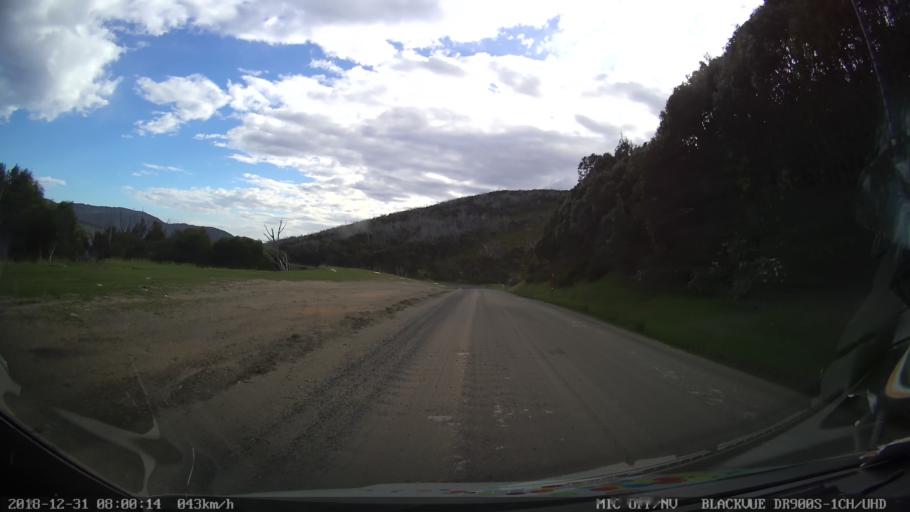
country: AU
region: New South Wales
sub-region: Snowy River
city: Jindabyne
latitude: -36.3690
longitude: 148.3902
